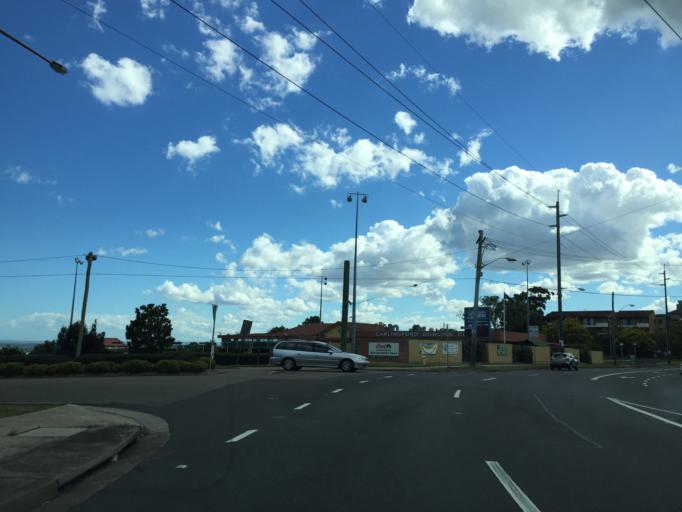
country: AU
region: New South Wales
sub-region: Parramatta
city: Carlingford
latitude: -33.7822
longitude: 151.0501
